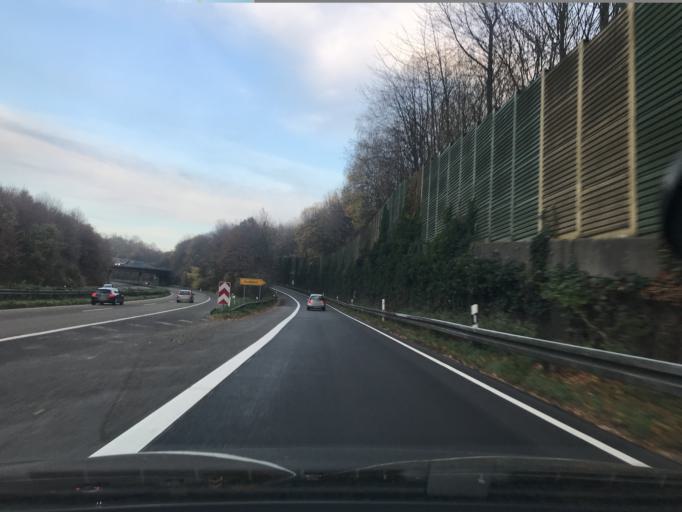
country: DE
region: North Rhine-Westphalia
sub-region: Regierungsbezirk Dusseldorf
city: Solingen
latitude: 51.1708
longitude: 7.0592
